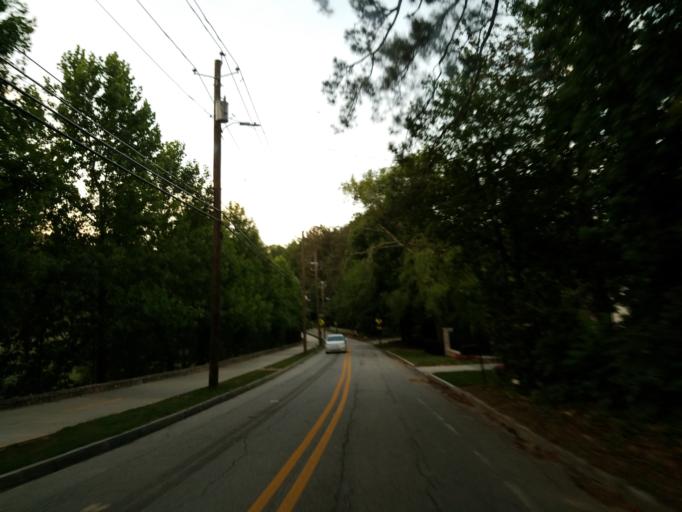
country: US
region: Georgia
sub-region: DeKalb County
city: North Atlanta
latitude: 33.8642
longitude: -84.3914
